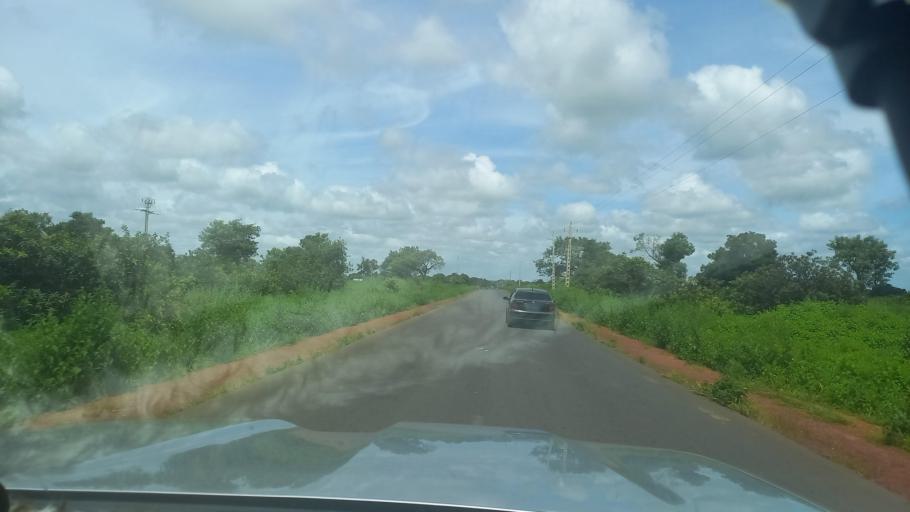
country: GM
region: Lower River
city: Kaiaf
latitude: 13.1943
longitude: -15.5544
